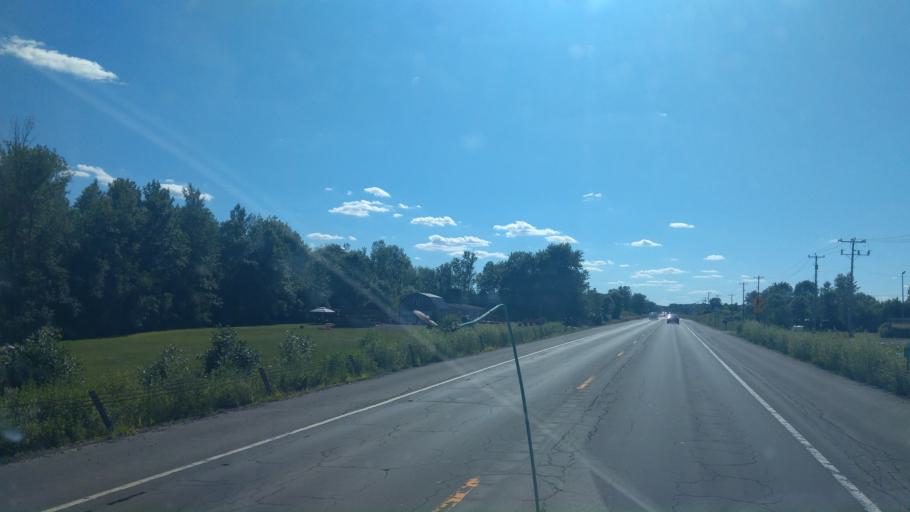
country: US
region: New York
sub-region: Seneca County
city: Waterloo
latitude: 42.9545
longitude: -76.9107
